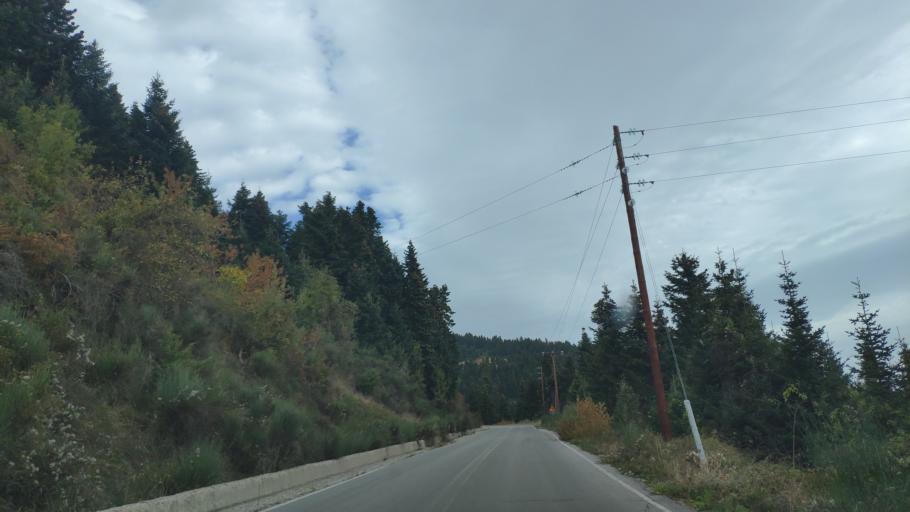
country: GR
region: Central Greece
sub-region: Nomos Fokidos
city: Amfissa
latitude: 38.6956
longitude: 22.3172
